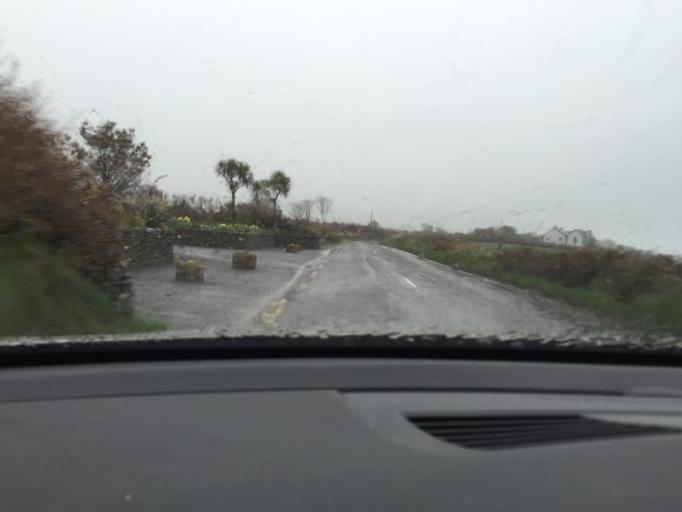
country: IE
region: Munster
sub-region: Ciarrai
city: Dingle
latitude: 52.1307
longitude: -10.3495
